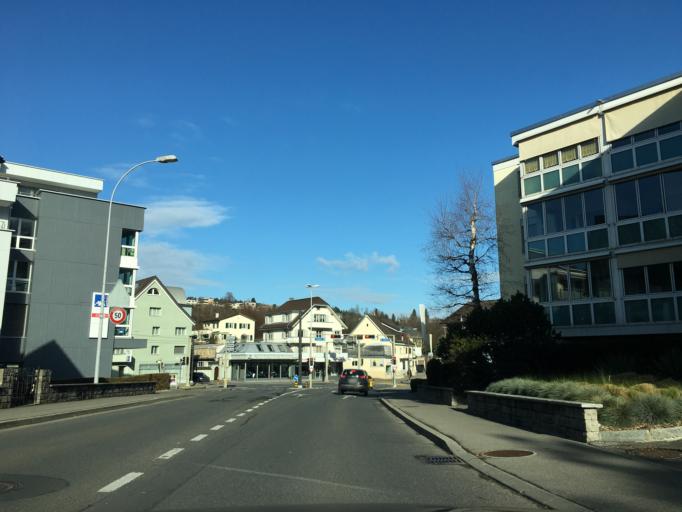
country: CH
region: Lucerne
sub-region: Lucerne-Land District
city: Ebikon
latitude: 47.0787
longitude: 8.3374
